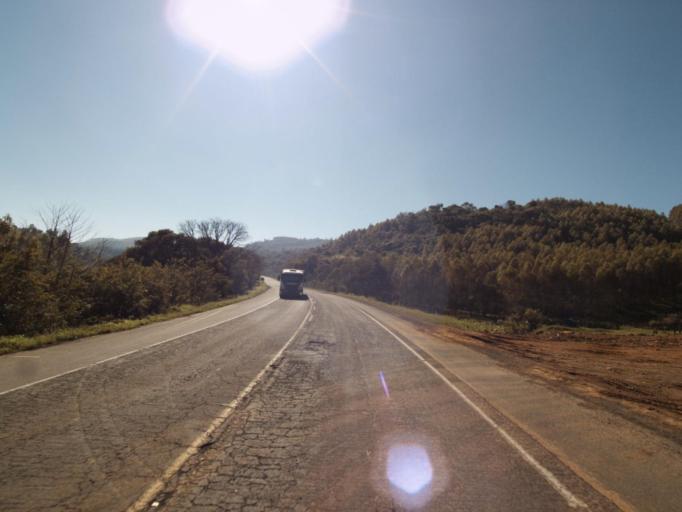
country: BR
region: Rio Grande do Sul
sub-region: Frederico Westphalen
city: Frederico Westphalen
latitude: -27.0162
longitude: -53.2278
